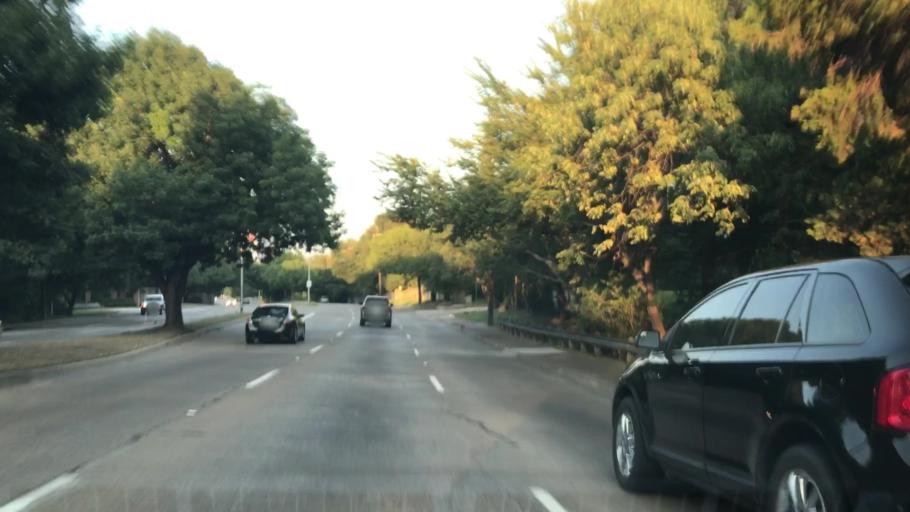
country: US
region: Texas
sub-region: Dallas County
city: University Park
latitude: 32.9093
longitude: -96.7961
